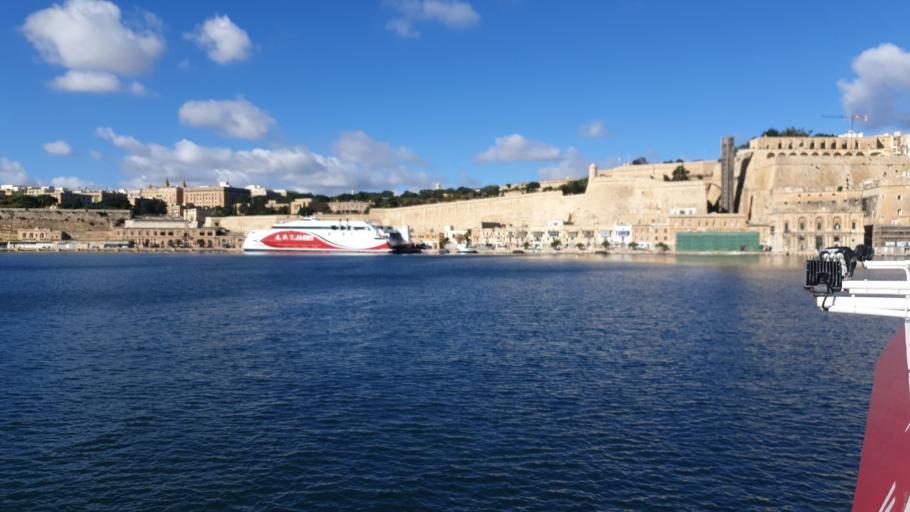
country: MT
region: Il-Birgu
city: Vittoriosa
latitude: 35.8916
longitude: 14.5150
